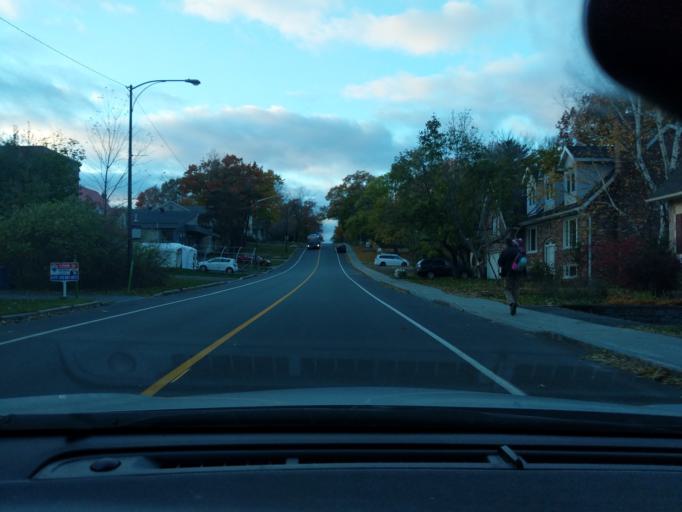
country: CA
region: Quebec
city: Quebec
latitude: 46.7696
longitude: -71.2671
